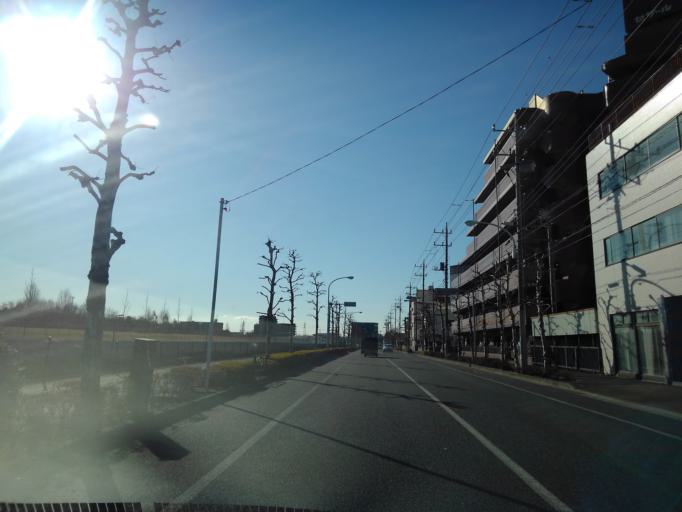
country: JP
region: Tokyo
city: Fussa
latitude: 35.7342
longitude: 139.3830
